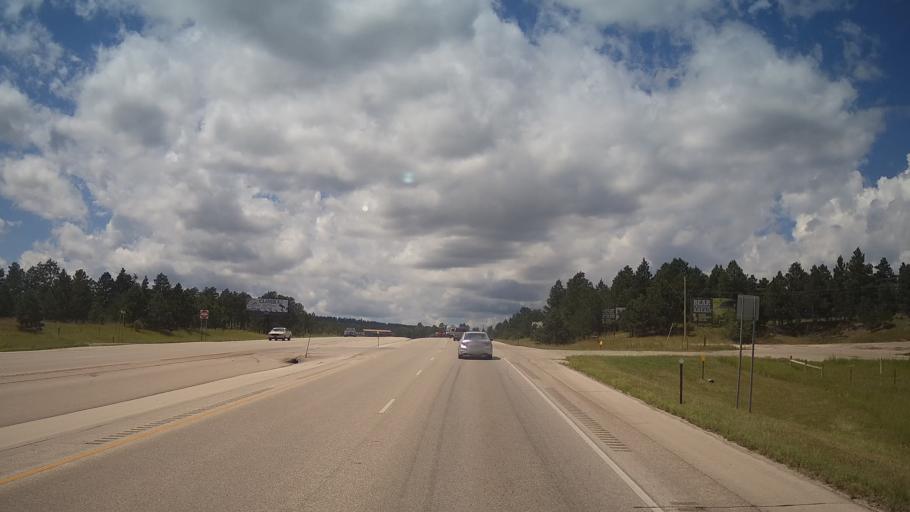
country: US
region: South Dakota
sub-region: Pennington County
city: Colonial Pine Hills
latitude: 43.9740
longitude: -103.2905
